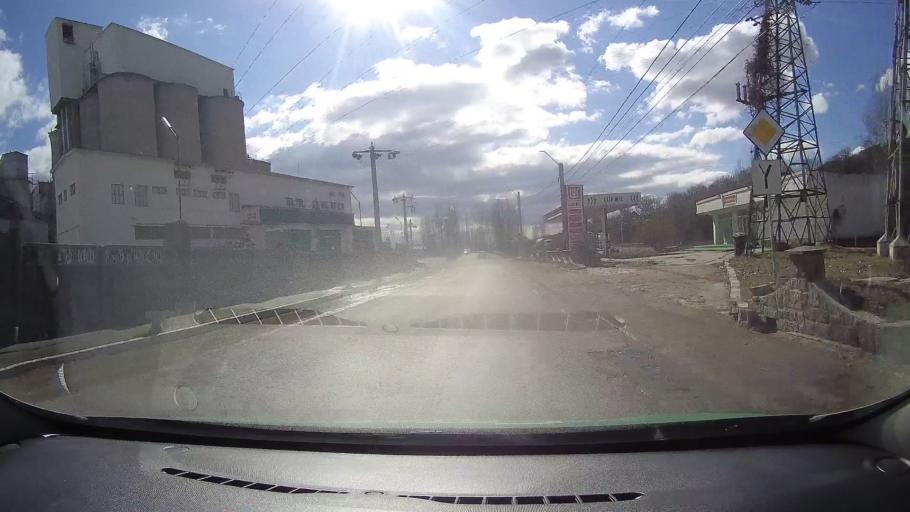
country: RO
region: Dambovita
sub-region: Comuna Fieni
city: Fieni
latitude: 45.1215
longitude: 25.4151
